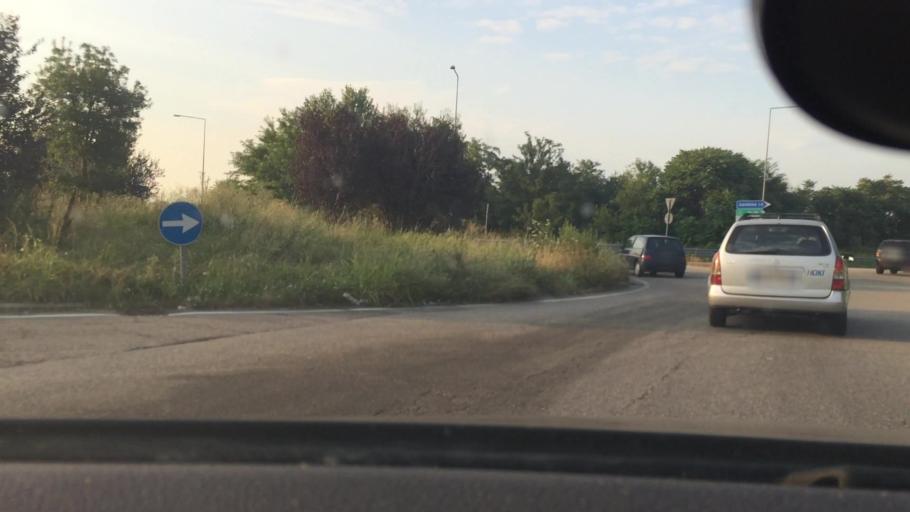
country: IT
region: Lombardy
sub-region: Citta metropolitana di Milano
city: Casorezzo
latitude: 45.5166
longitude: 8.9108
